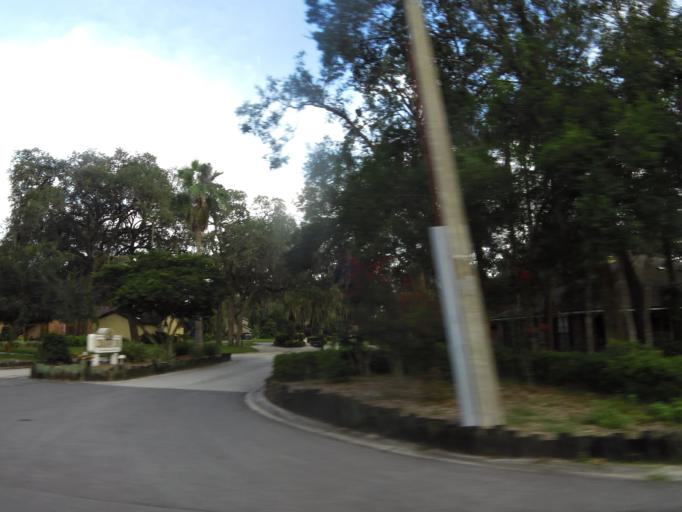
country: US
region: Florida
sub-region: Saint Johns County
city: Fruit Cove
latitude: 30.1406
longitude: -81.6251
